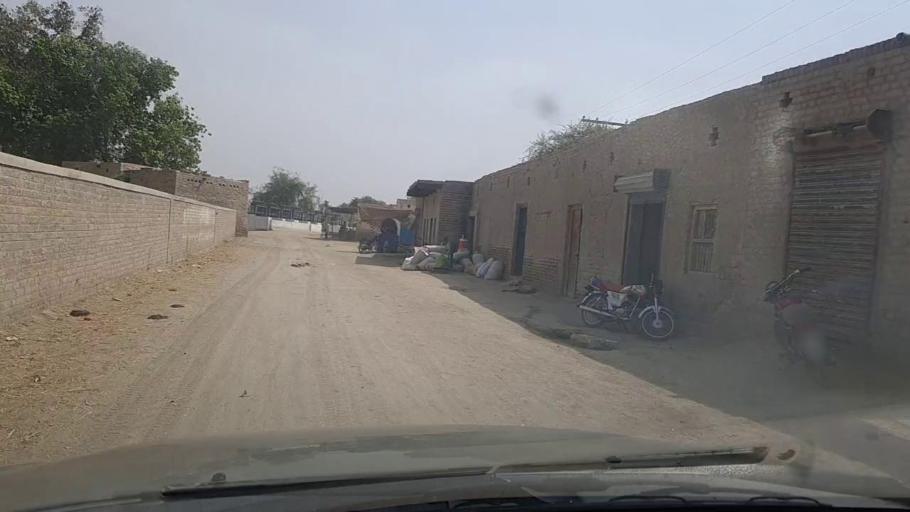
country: PK
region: Sindh
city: Lakhi
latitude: 27.9110
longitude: 68.6880
